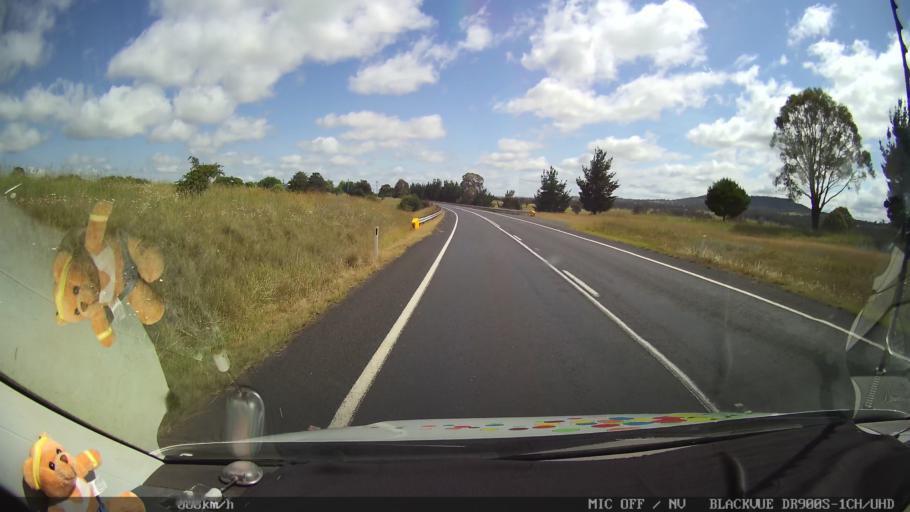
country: AU
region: New South Wales
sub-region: Glen Innes Severn
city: Glen Innes
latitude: -29.8856
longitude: 151.7339
